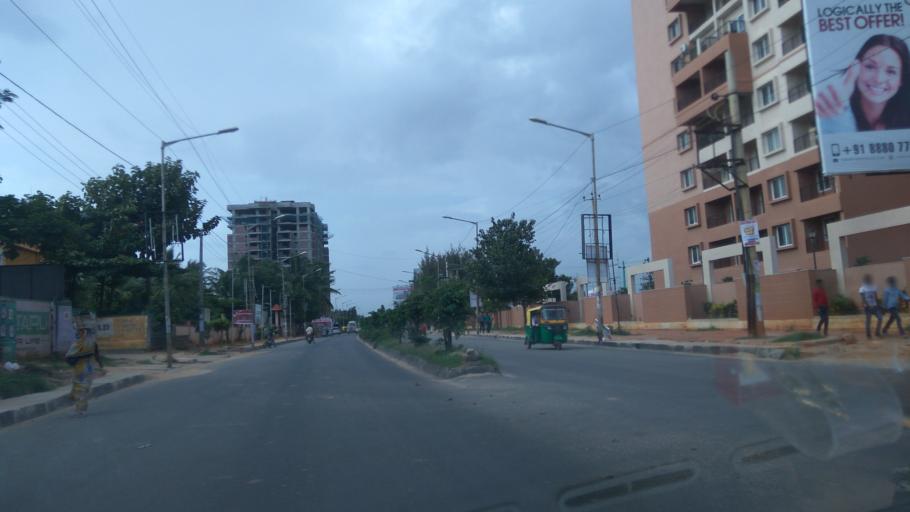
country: IN
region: Karnataka
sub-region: Bangalore Urban
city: Yelahanka
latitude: 13.0775
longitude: 77.6337
